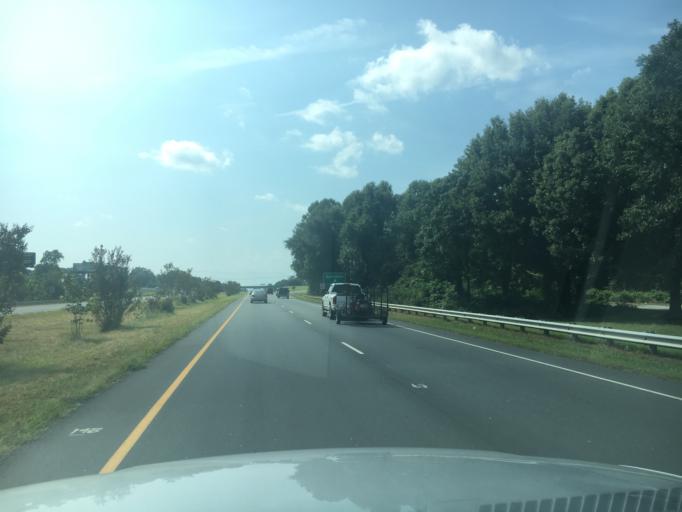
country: US
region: North Carolina
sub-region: Rutherford County
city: Spindale
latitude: 35.3412
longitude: -81.9137
